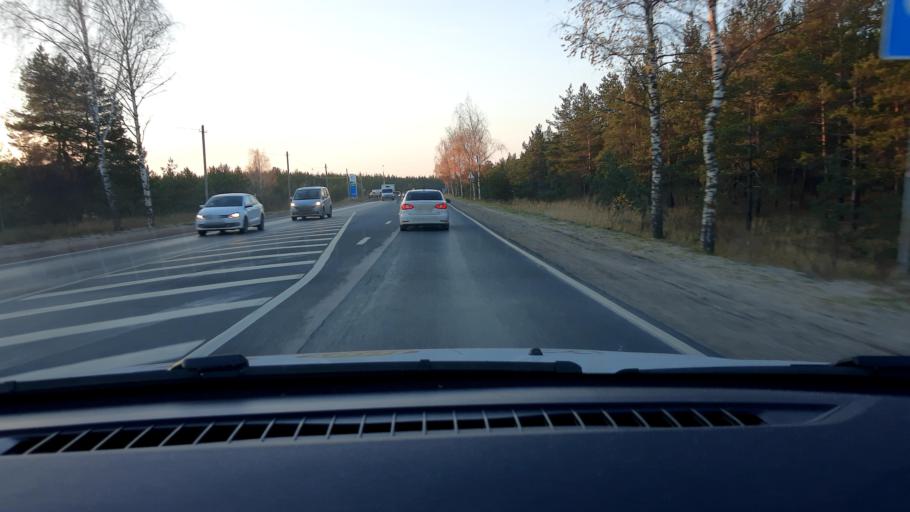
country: RU
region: Nizjnij Novgorod
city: Dzerzhinsk
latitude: 56.2793
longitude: 43.4751
